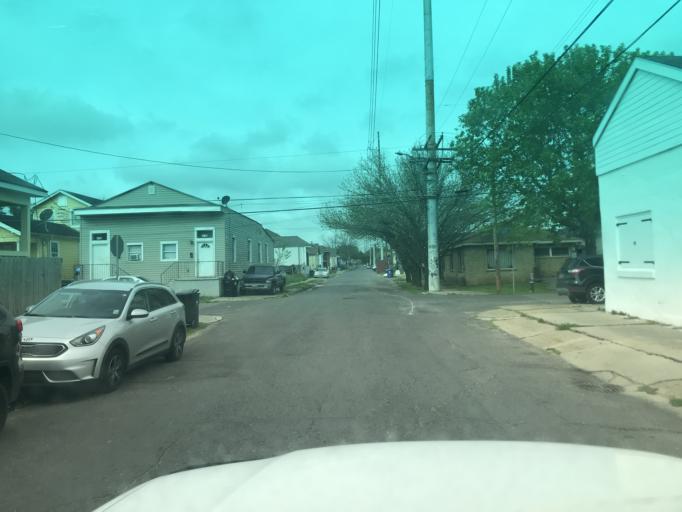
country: US
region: Louisiana
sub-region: Orleans Parish
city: New Orleans
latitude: 29.9759
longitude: -90.0535
